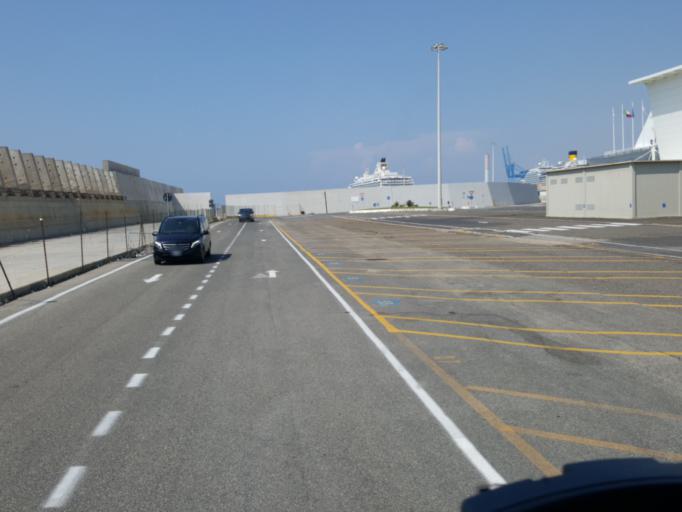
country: IT
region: Latium
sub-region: Citta metropolitana di Roma Capitale
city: Civitavecchia
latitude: 42.0946
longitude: 11.7776
